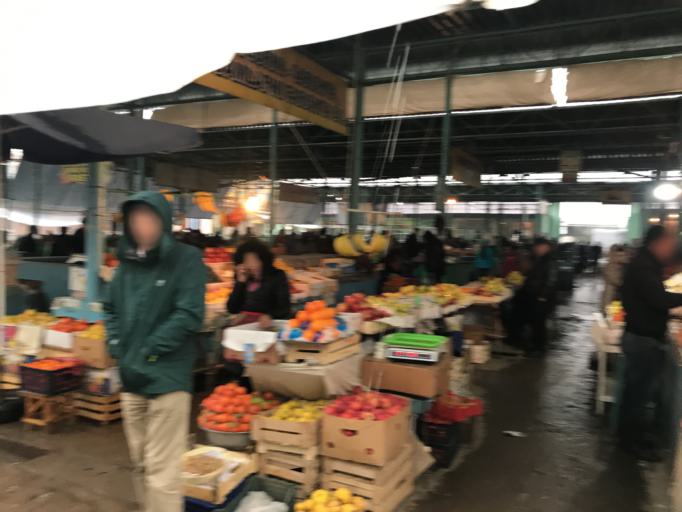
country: UZ
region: Toshkent
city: Yangiyul
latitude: 41.1173
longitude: 69.0544
